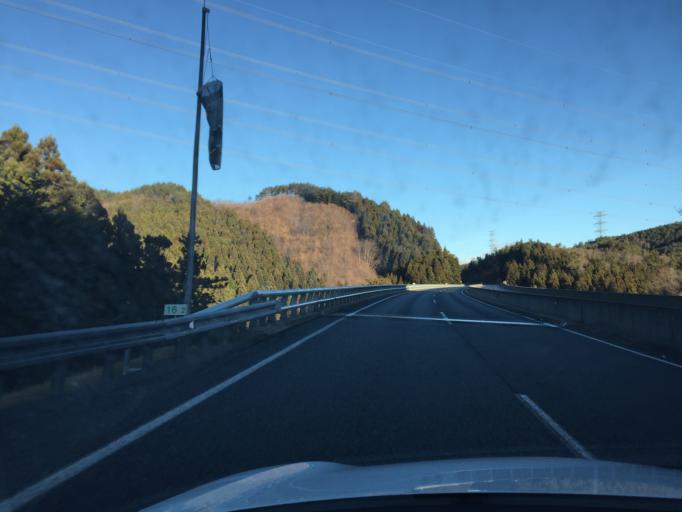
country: JP
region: Fukushima
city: Iwaki
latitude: 37.1565
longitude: 140.7331
